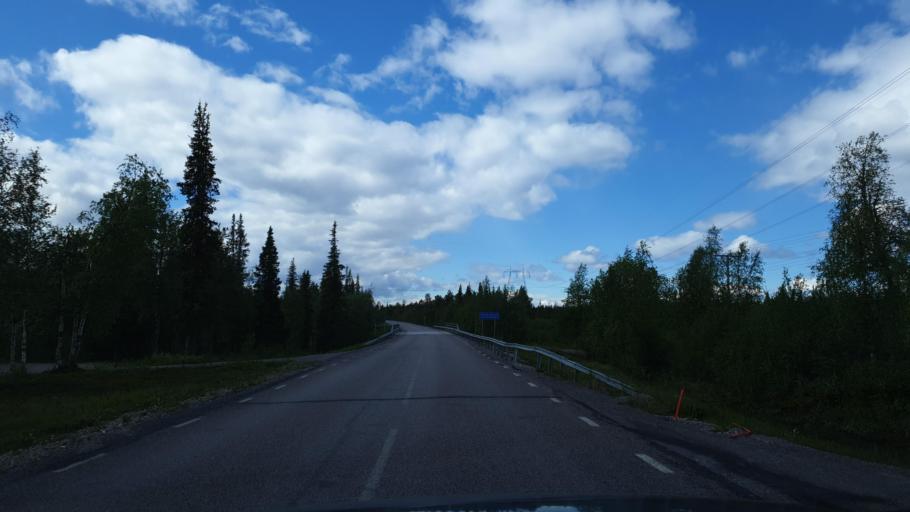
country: SE
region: Norrbotten
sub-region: Jokkmokks Kommun
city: Jokkmokk
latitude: 67.1007
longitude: 19.7400
